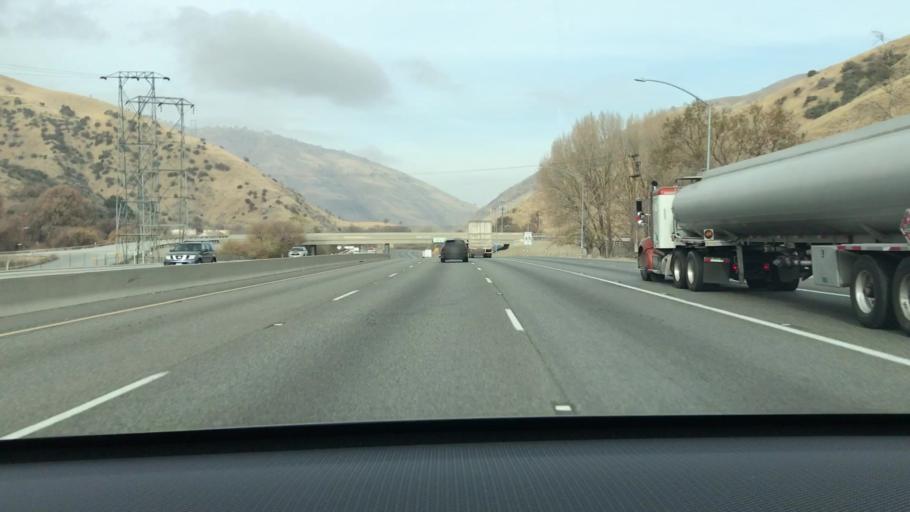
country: US
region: California
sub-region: Kern County
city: Lebec
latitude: 34.8751
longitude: -118.8923
